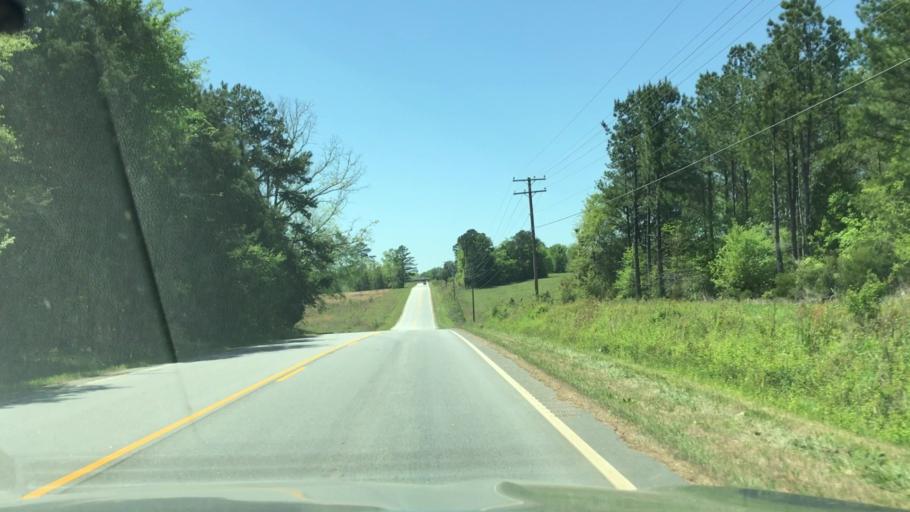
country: US
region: South Carolina
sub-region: Union County
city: Buffalo
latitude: 34.6834
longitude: -81.7157
